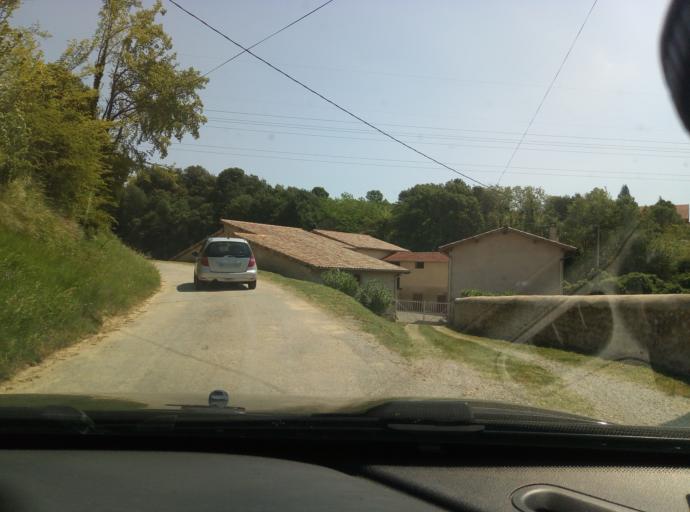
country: FR
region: Rhone-Alpes
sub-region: Departement de la Drome
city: Chanos-Curson
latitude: 45.0630
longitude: 4.9164
